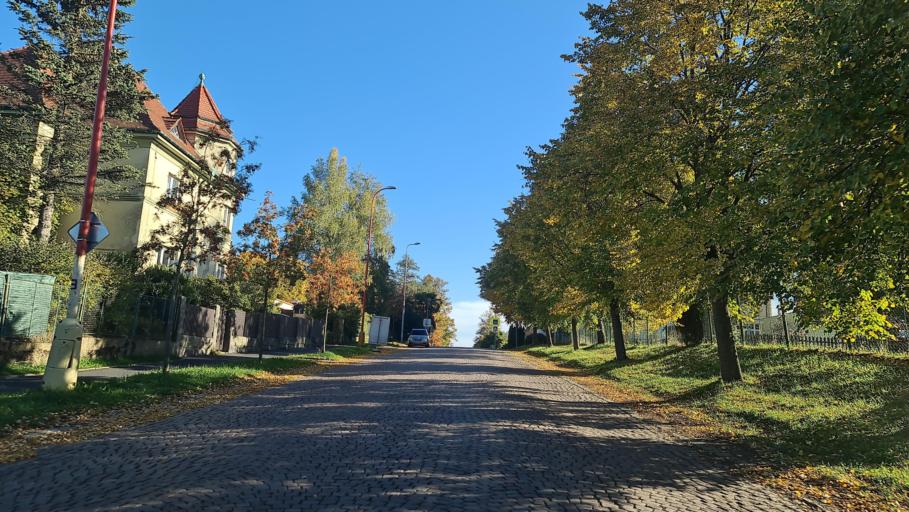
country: CZ
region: Karlovarsky
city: As
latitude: 50.2224
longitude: 12.1788
